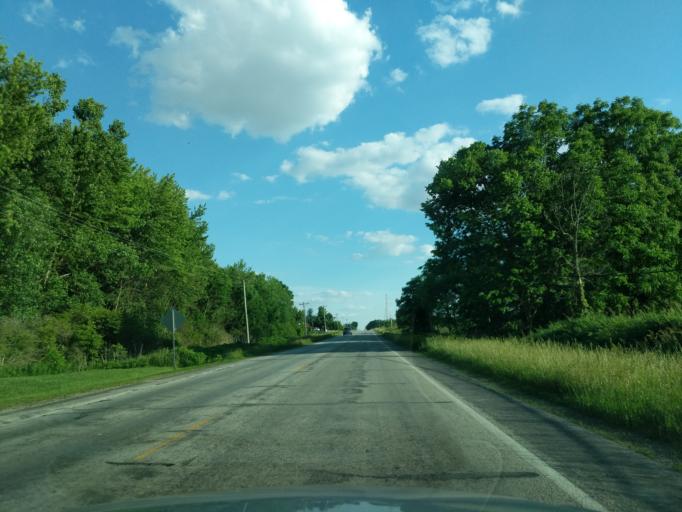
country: US
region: Indiana
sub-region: Whitley County
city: Columbia City
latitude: 41.1134
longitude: -85.4715
